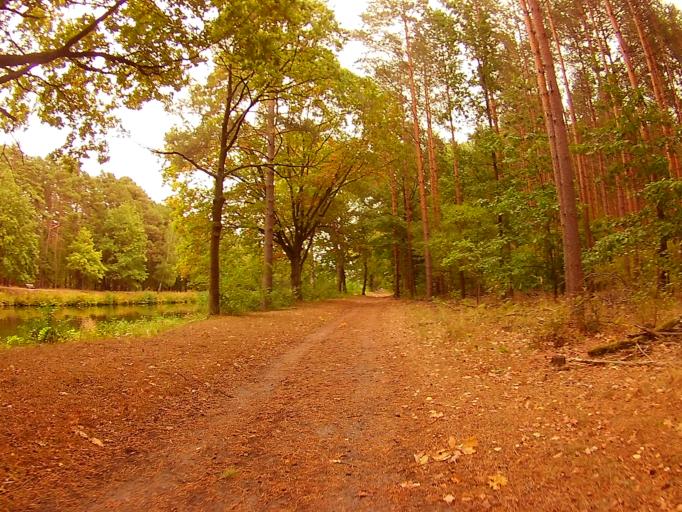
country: DE
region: Berlin
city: Schmockwitz
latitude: 52.3768
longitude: 13.6822
